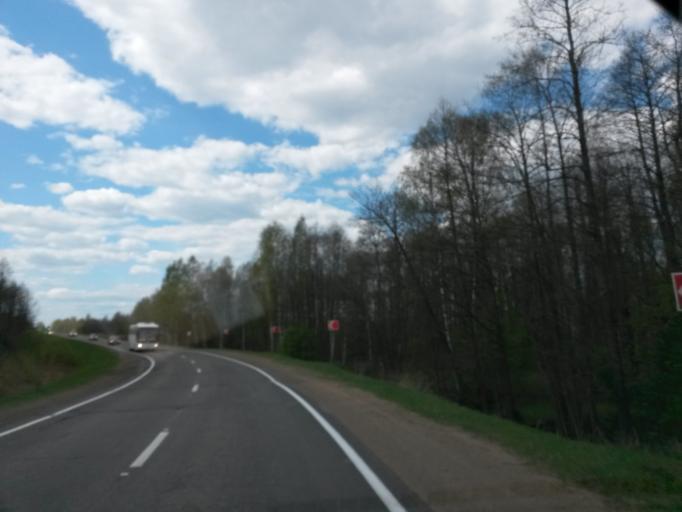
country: RU
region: Jaroslavl
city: Kurba
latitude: 57.6888
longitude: 39.2297
